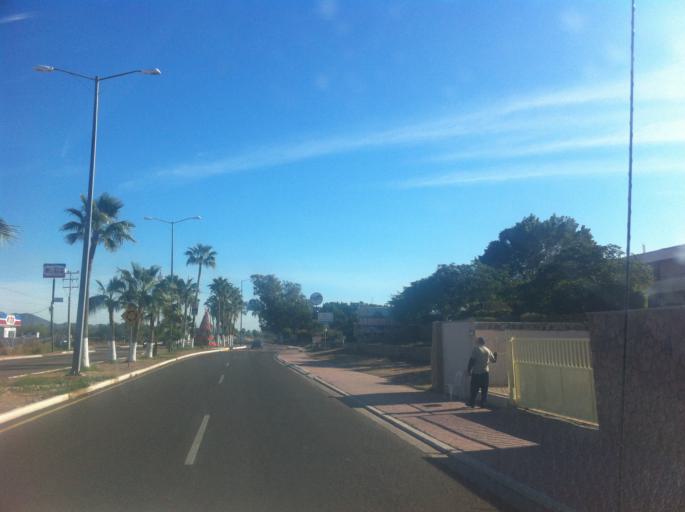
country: MX
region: Sonora
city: Heroica Guaymas
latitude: 27.9639
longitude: -111.0216
